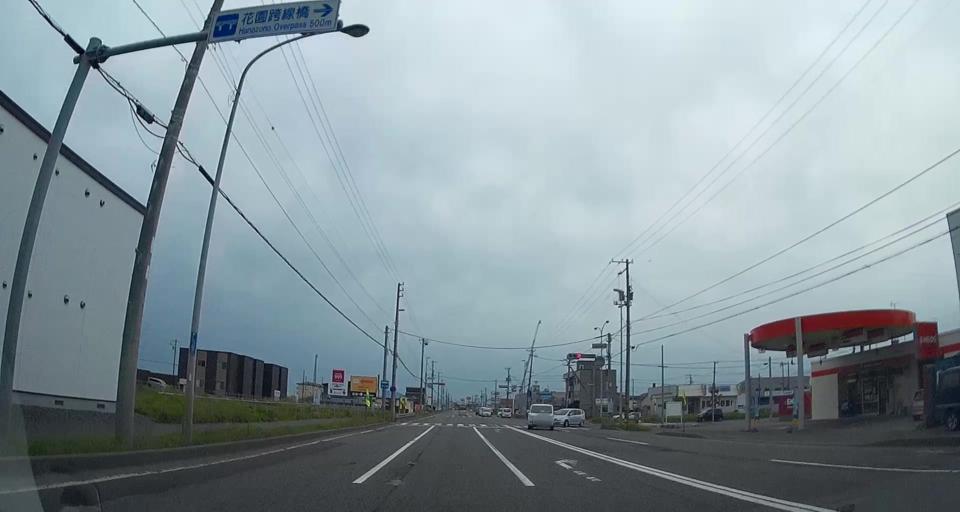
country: JP
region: Hokkaido
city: Tomakomai
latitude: 42.6244
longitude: 141.5793
